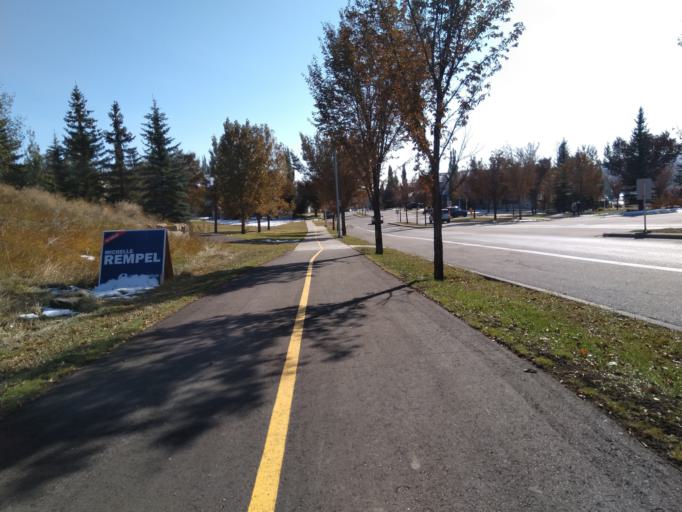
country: CA
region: Alberta
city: Calgary
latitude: 51.1571
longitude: -114.1010
